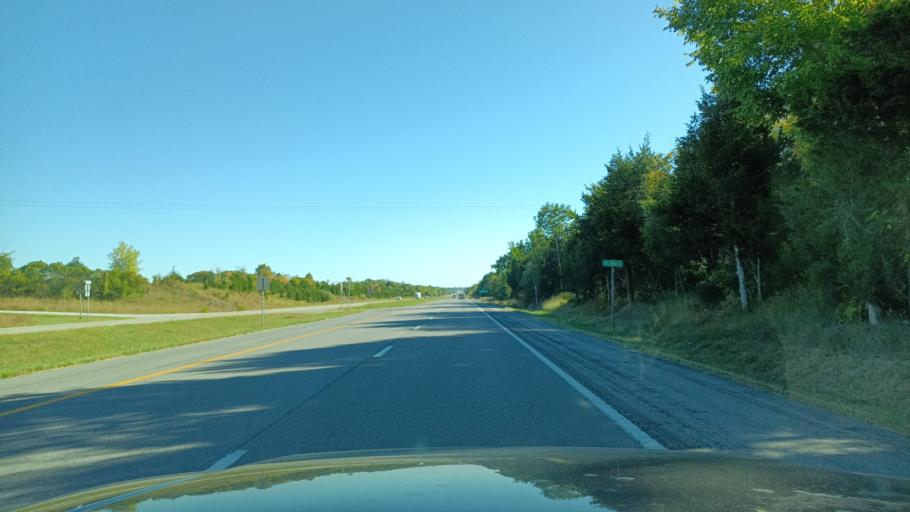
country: US
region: Missouri
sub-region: Boone County
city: Hallsville
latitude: 39.0926
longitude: -92.3298
